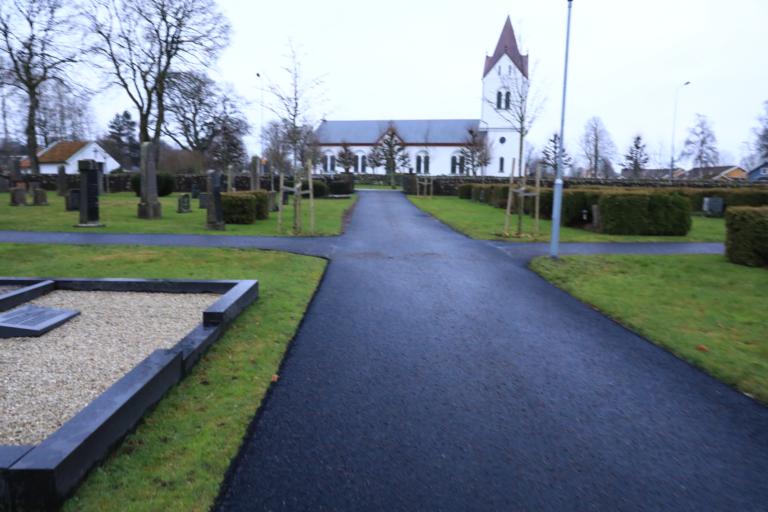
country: SE
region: Halland
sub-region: Varbergs Kommun
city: Tvaaker
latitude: 57.0468
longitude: 12.3999
